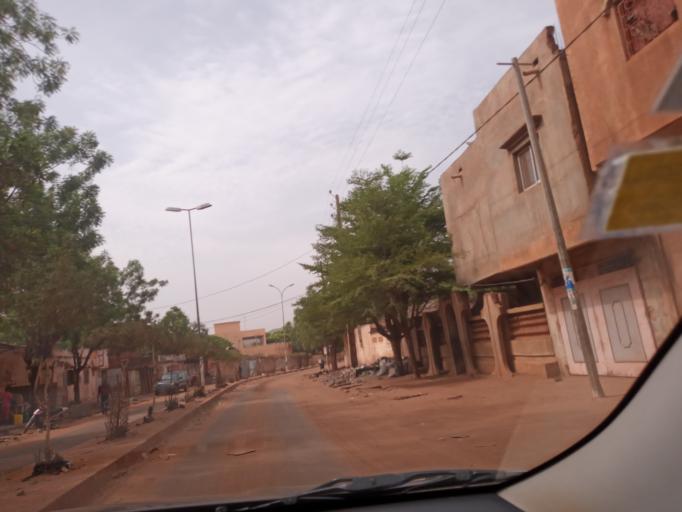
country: ML
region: Bamako
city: Bamako
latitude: 12.6773
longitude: -7.9244
